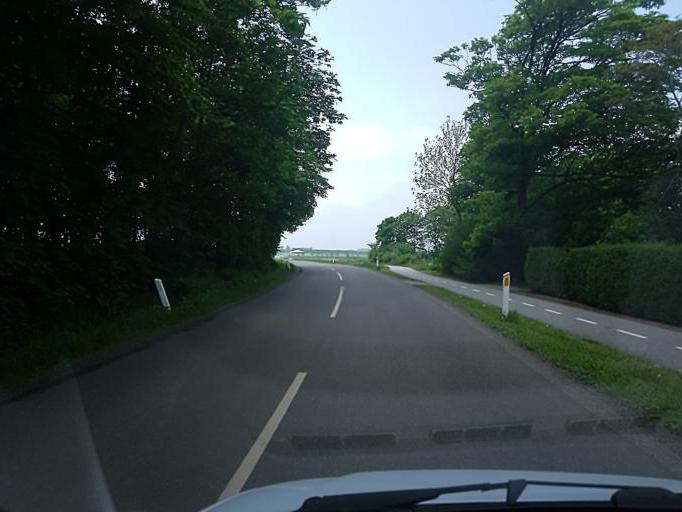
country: DK
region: South Denmark
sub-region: Varde Kommune
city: Varde
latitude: 55.5394
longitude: 8.5067
